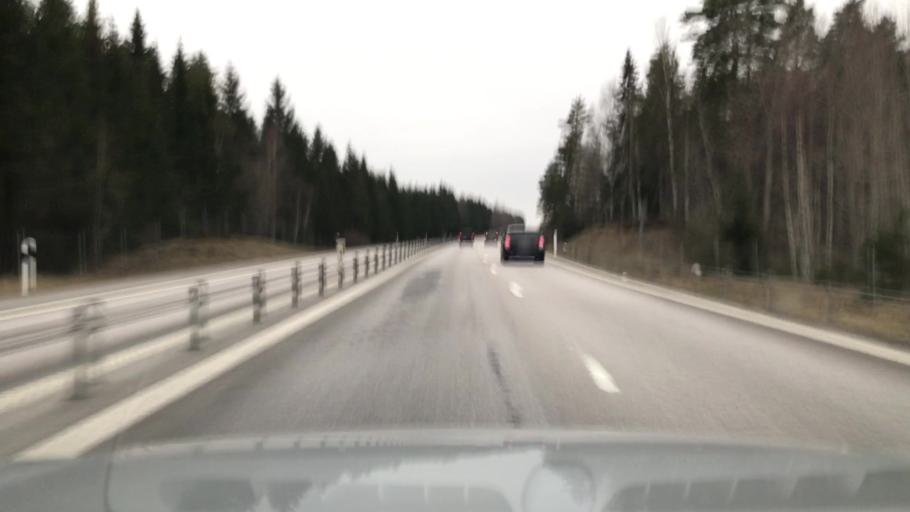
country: SE
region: OEstergoetland
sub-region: Valdemarsviks Kommun
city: Gusum
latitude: 58.2561
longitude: 16.5280
